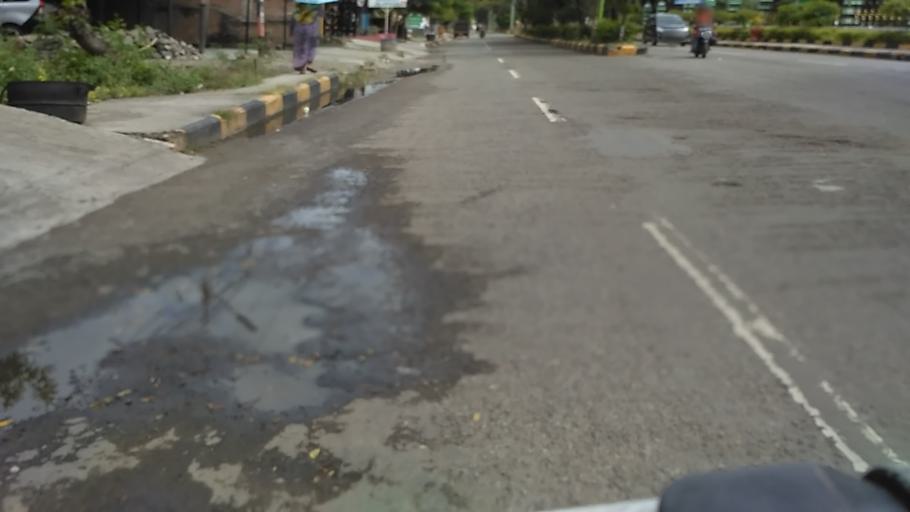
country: ID
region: South Sulawesi
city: Pinrang
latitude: -3.8113
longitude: 119.6511
